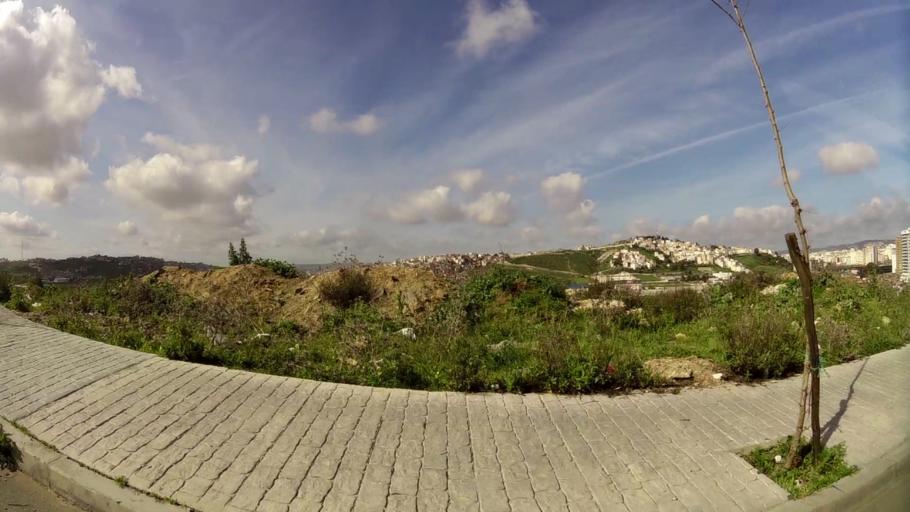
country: MA
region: Tanger-Tetouan
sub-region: Tanger-Assilah
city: Tangier
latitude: 35.7689
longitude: -5.7773
